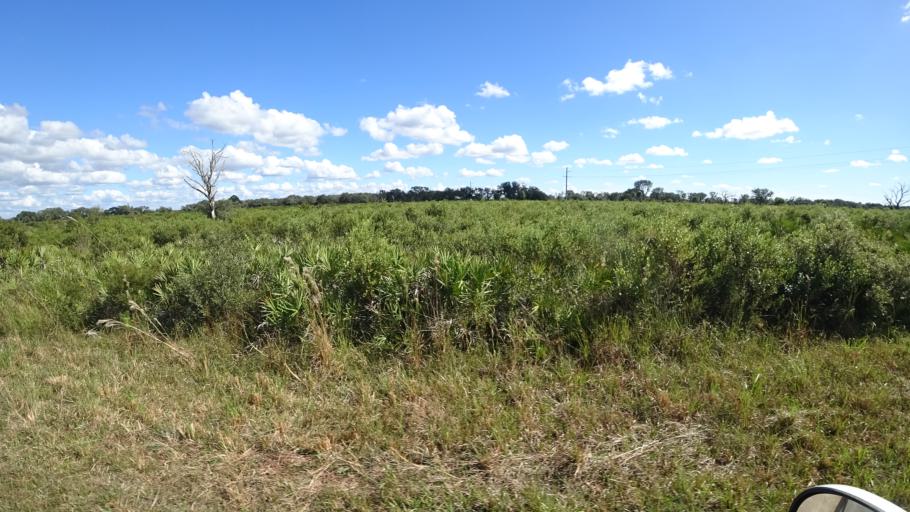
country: US
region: Florida
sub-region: Sarasota County
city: Lake Sarasota
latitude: 27.2489
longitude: -82.2833
